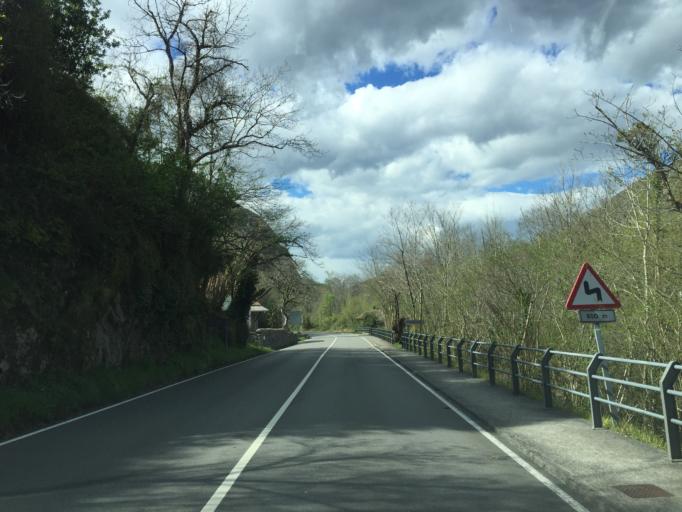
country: ES
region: Asturias
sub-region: Province of Asturias
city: Cangas de Onis
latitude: 43.3157
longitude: -5.0705
